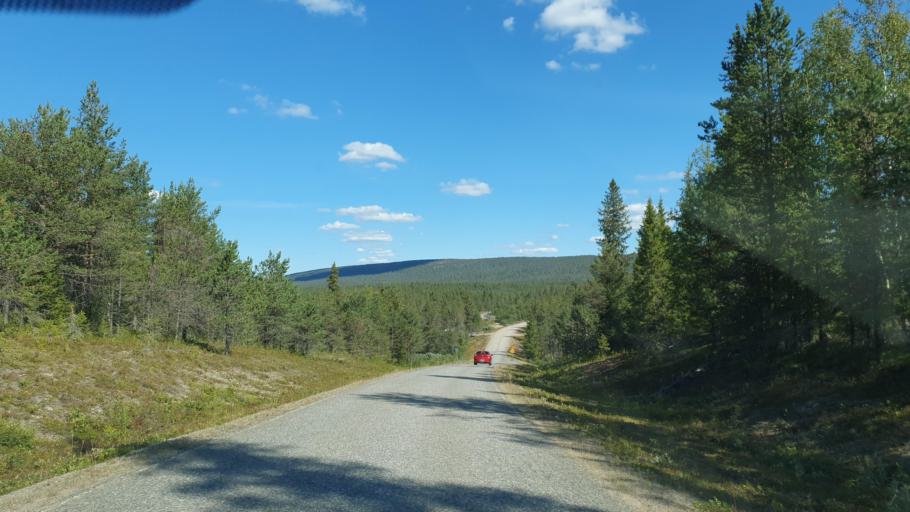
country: FI
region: Lapland
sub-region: Tunturi-Lappi
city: Muonio
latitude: 67.7029
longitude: 24.1202
